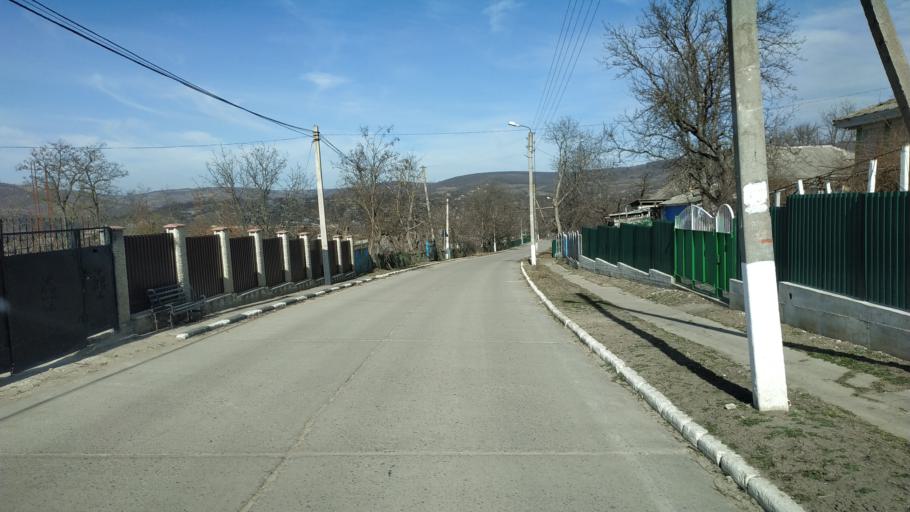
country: MD
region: Nisporeni
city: Nisporeni
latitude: 47.0730
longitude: 28.2612
